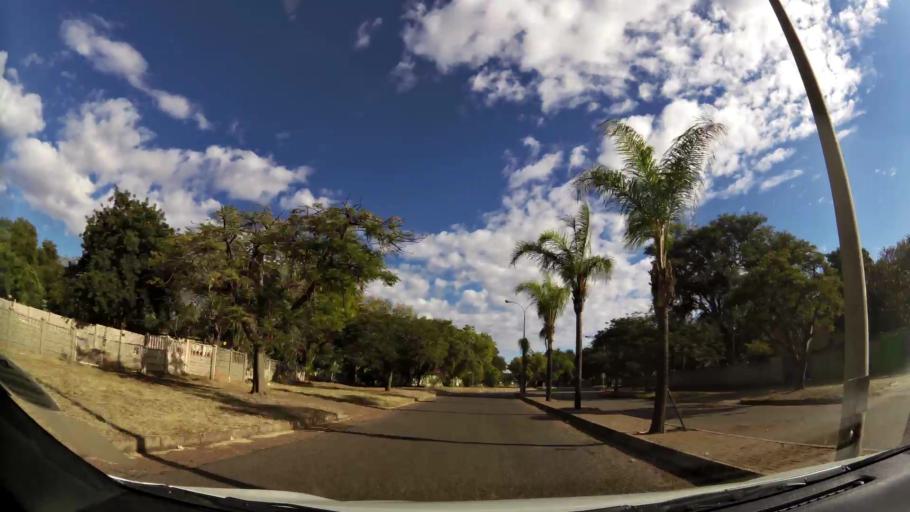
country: ZA
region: Limpopo
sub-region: Waterberg District Municipality
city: Warmbaths
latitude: -24.8835
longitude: 28.2807
